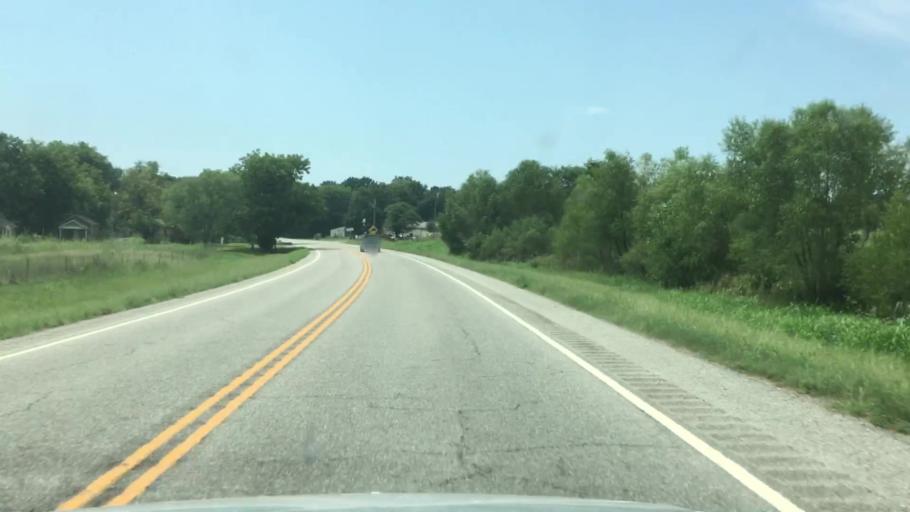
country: US
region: Oklahoma
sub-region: Muskogee County
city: Fort Gibson
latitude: 35.9362
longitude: -95.2259
